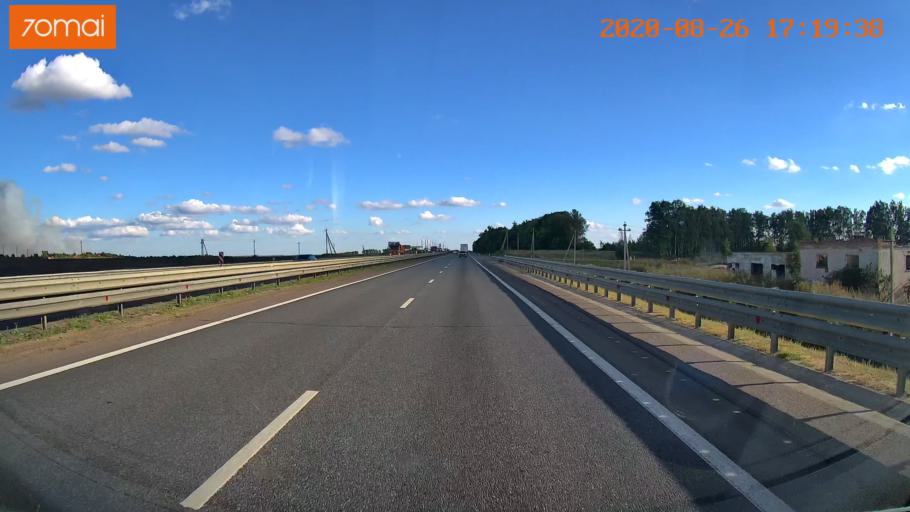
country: RU
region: Tula
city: Volovo
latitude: 53.5923
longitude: 38.1062
